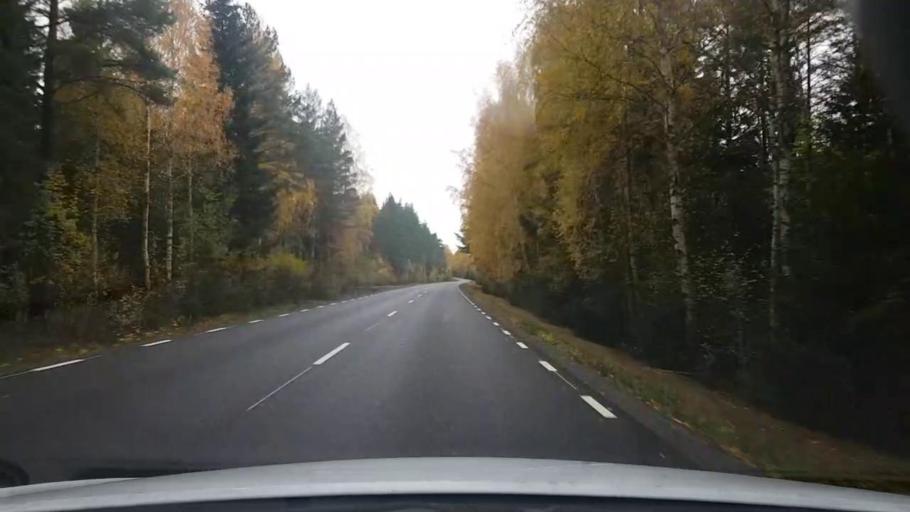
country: SE
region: OErebro
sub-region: Laxa Kommun
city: Laxa
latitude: 58.7880
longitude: 14.5395
